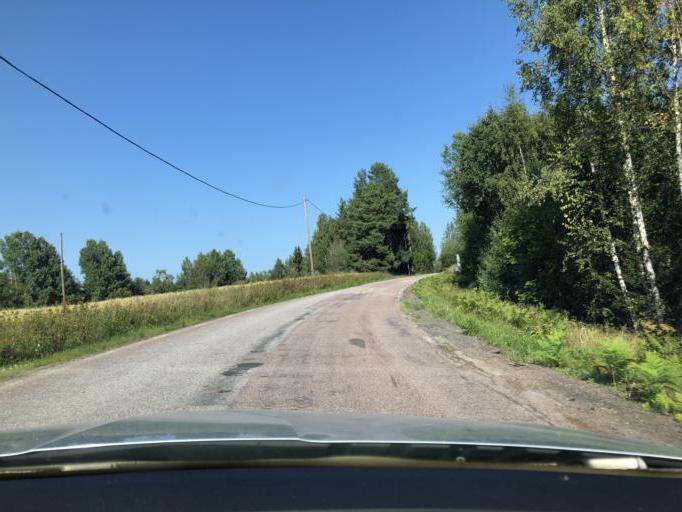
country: SE
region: Dalarna
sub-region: Hedemora Kommun
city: Hedemora
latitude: 60.3260
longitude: 15.9141
